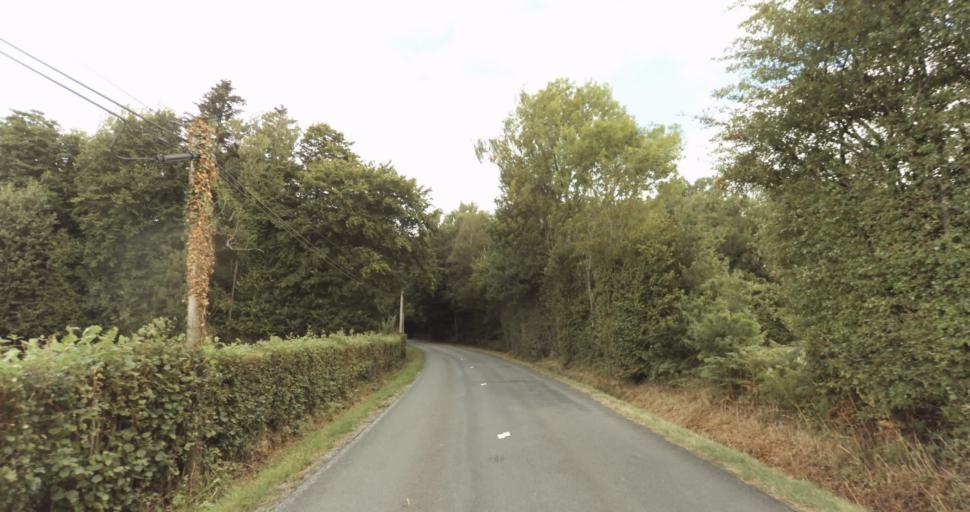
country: FR
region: Lower Normandy
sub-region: Departement de l'Orne
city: Gace
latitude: 48.7981
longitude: 0.2595
